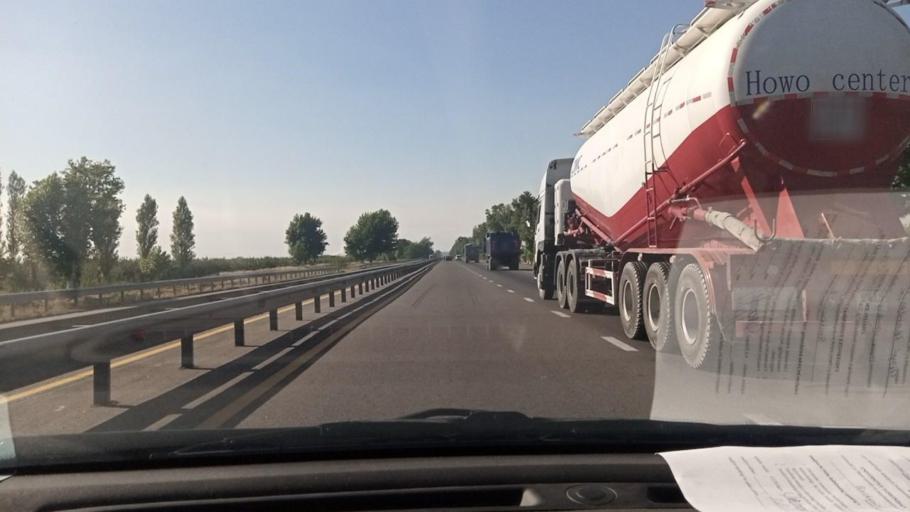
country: UZ
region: Toshkent Shahri
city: Bektemir
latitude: 41.1738
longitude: 69.4118
